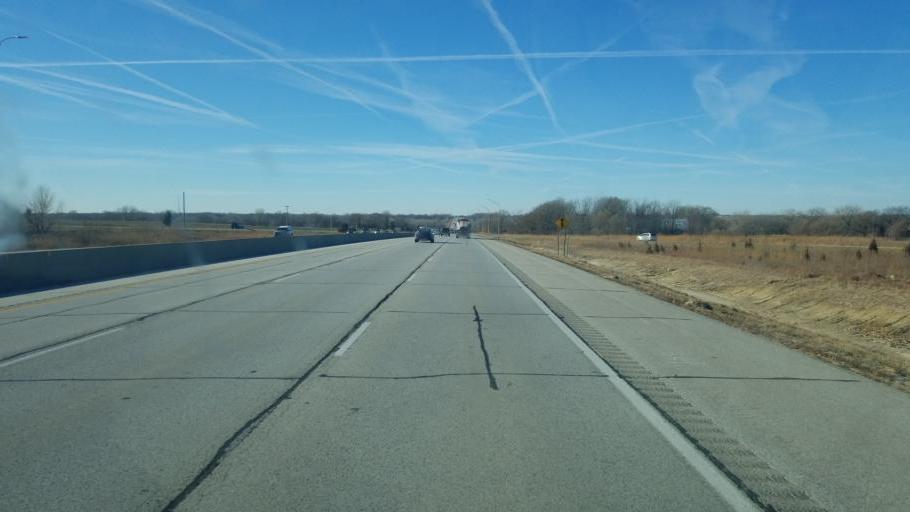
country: US
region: Iowa
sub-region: Polk County
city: Altoona
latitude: 41.6593
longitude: -93.5281
